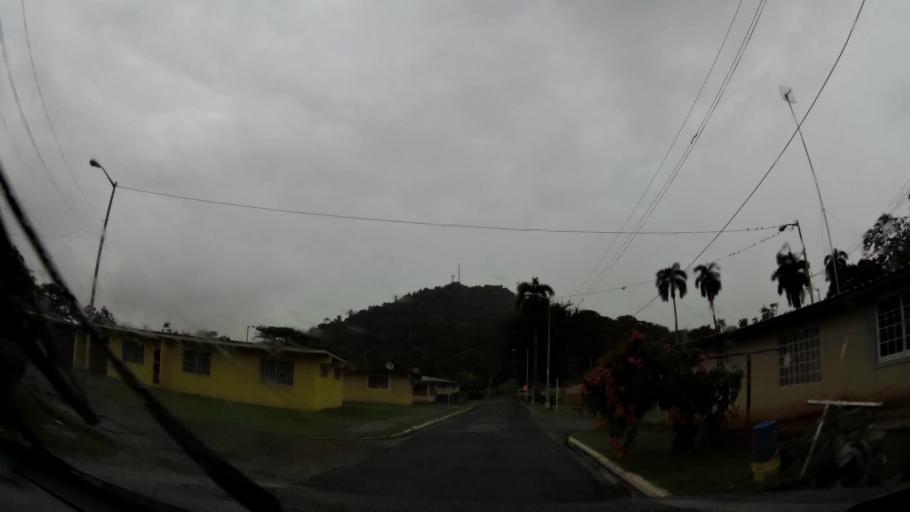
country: PA
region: Panama
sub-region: Distrito de Panama
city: Paraiso
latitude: 9.0194
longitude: -79.6099
